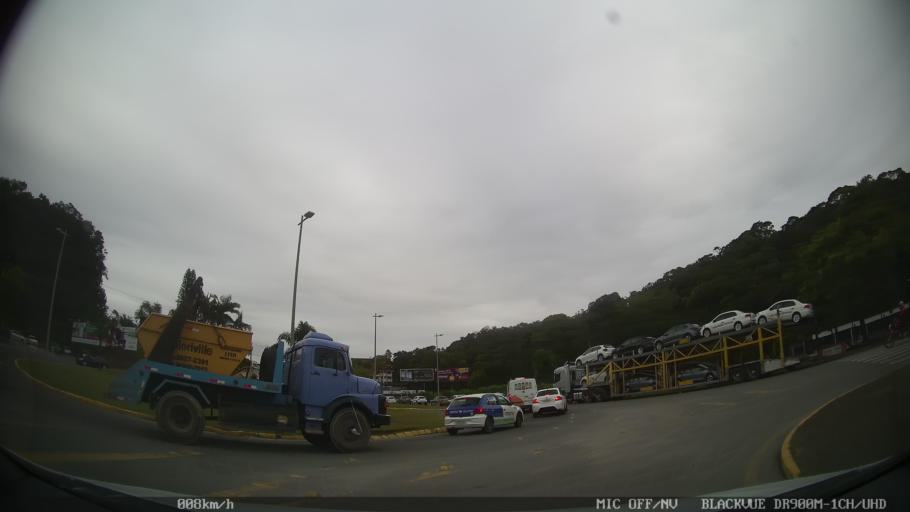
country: BR
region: Santa Catarina
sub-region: Joinville
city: Joinville
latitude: -26.2966
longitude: -48.8817
